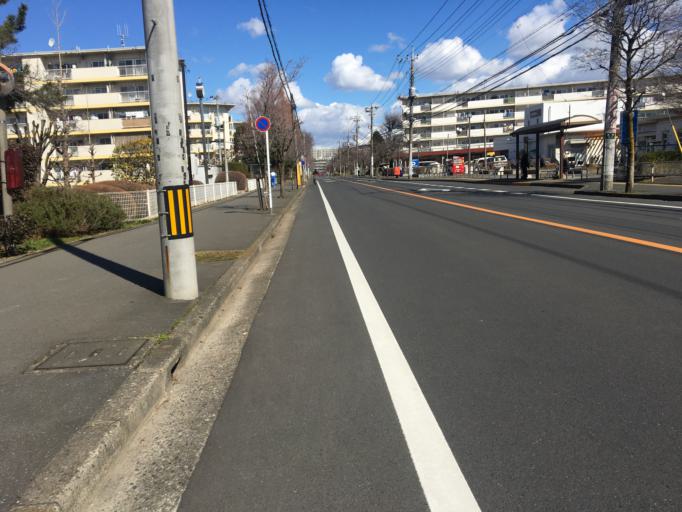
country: JP
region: Saitama
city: Shiki
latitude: 35.8213
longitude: 139.5561
